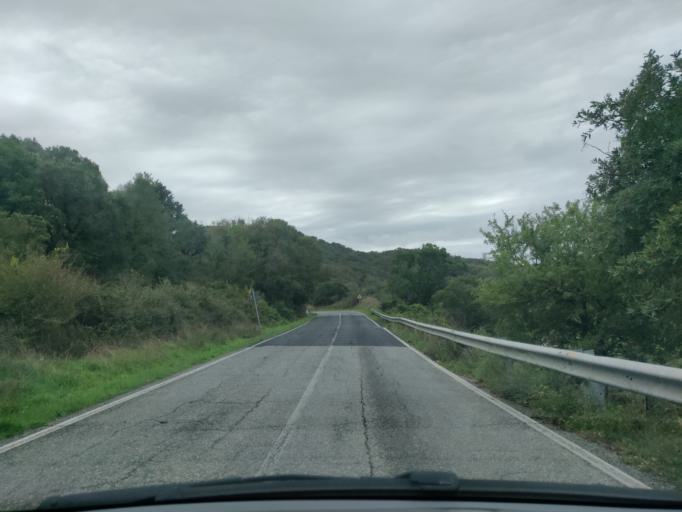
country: IT
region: Latium
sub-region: Citta metropolitana di Roma Capitale
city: Allumiere
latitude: 42.1452
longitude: 11.8797
